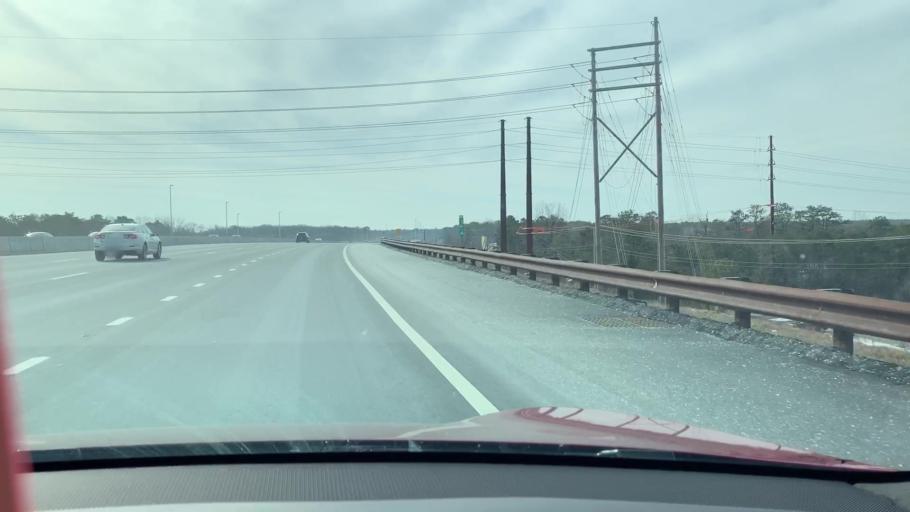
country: US
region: New Jersey
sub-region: Atlantic County
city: Northfield
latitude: 39.4028
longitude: -74.5582
